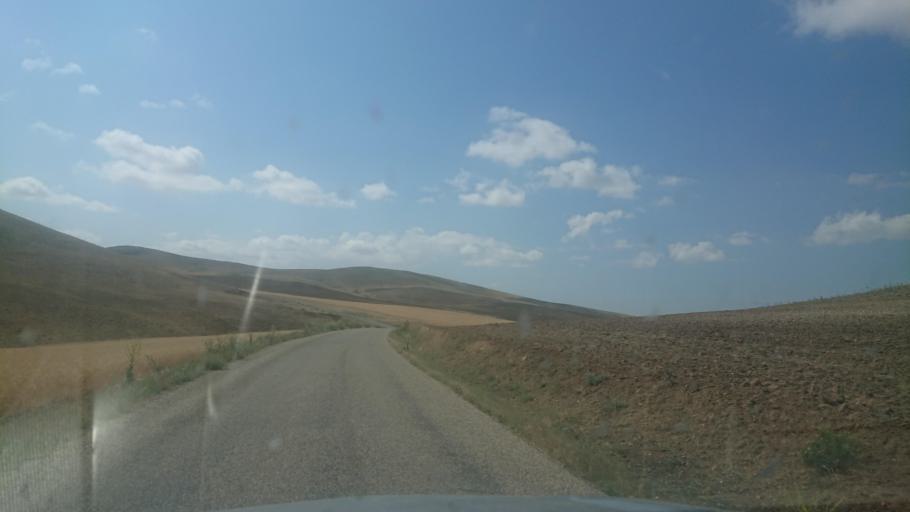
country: TR
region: Aksaray
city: Sariyahsi
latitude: 39.0096
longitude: 33.9491
